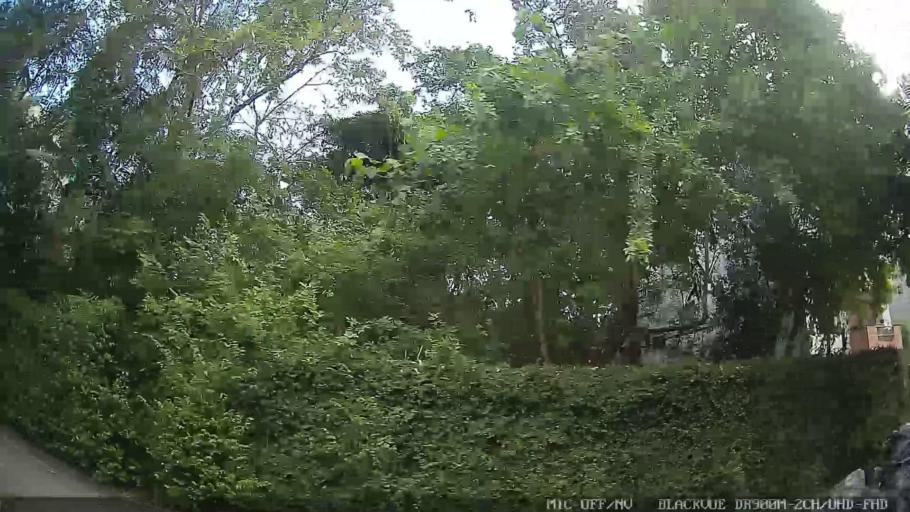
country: BR
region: Sao Paulo
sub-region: Guaruja
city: Guaruja
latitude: -23.9870
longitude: -46.2478
